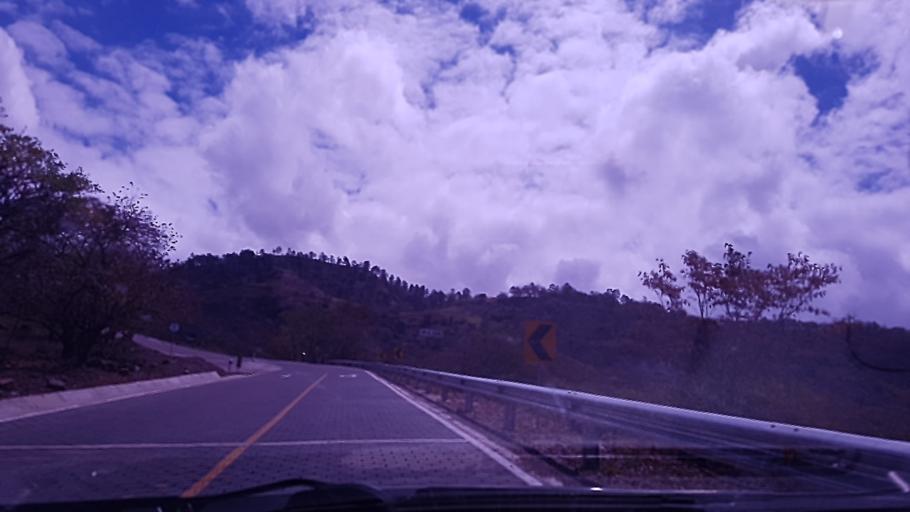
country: NI
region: Esteli
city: Condega
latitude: 13.4082
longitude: -86.2912
